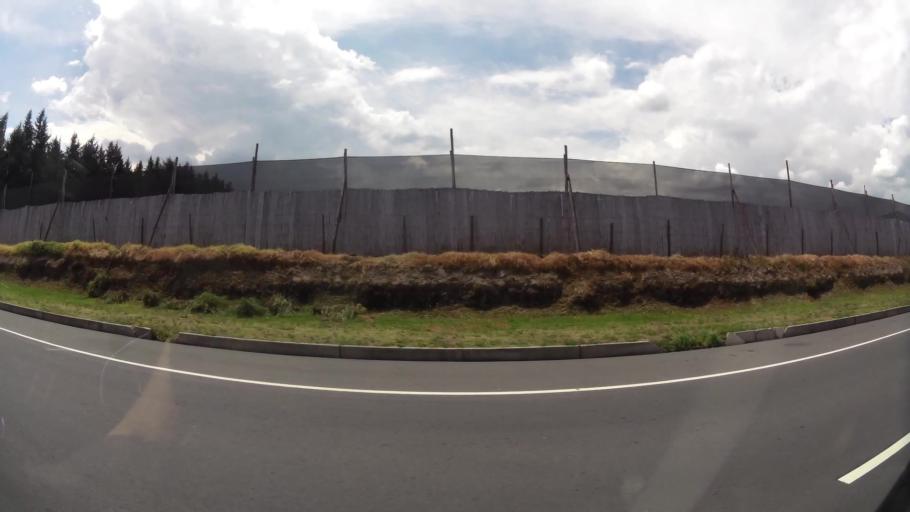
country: EC
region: Pichincha
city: Quito
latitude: -0.1584
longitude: -78.3481
